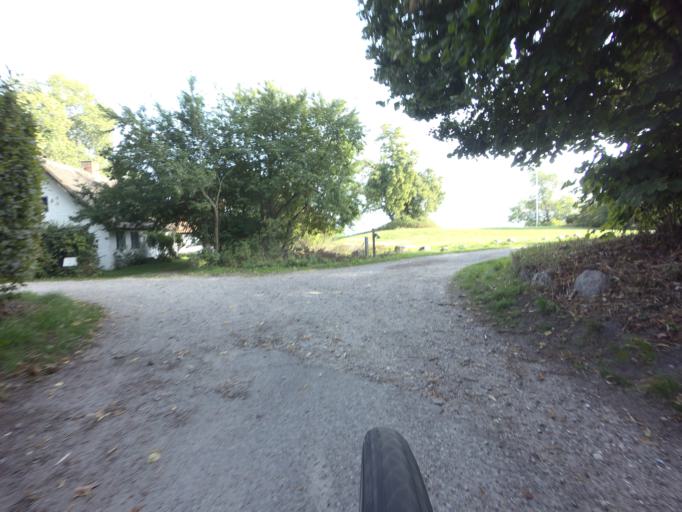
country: DK
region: Zealand
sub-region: Faxe Kommune
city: Fakse Ladeplads
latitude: 55.2370
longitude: 12.2394
